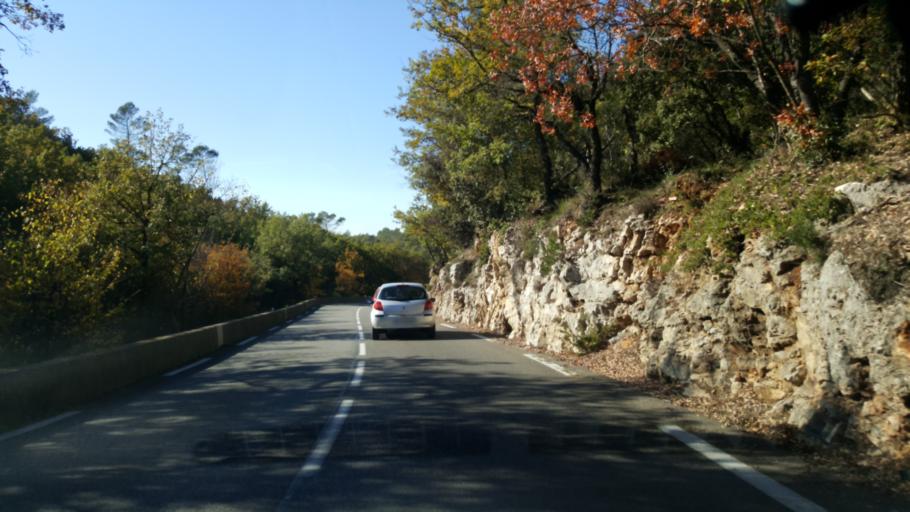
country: FR
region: Provence-Alpes-Cote d'Azur
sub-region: Departement du Var
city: Nans-les-Pins
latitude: 43.3854
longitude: 5.7492
